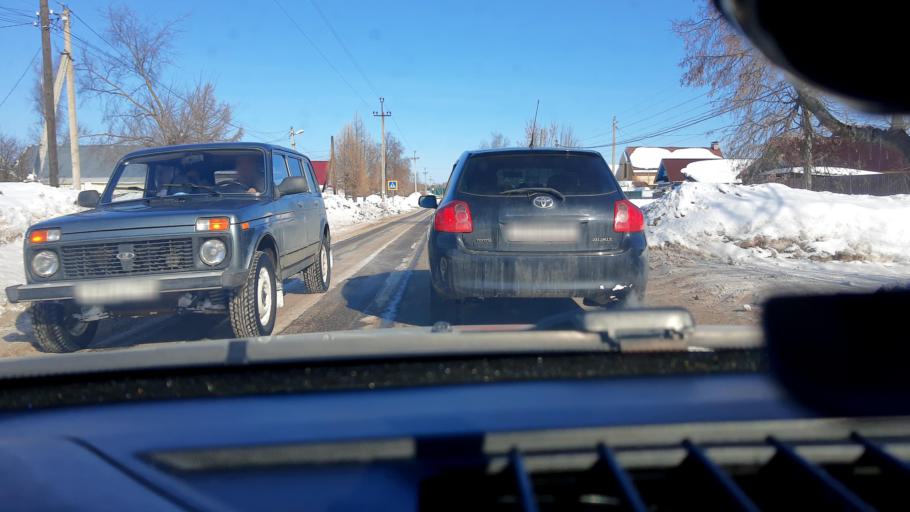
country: RU
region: Nizjnij Novgorod
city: Volodarsk
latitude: 56.2298
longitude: 43.2115
